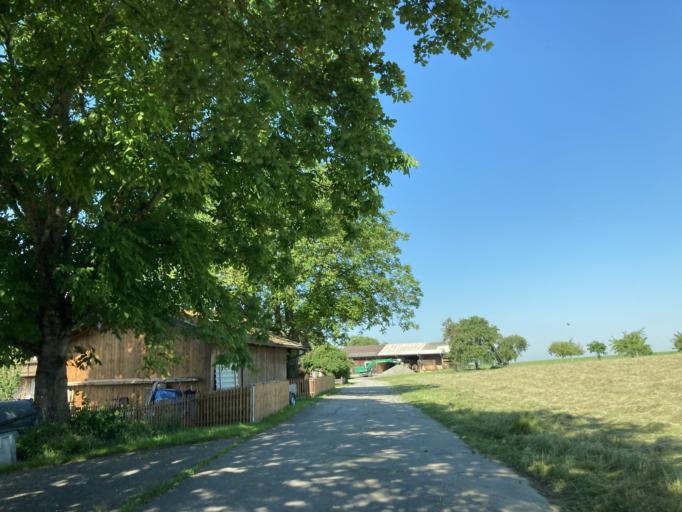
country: DE
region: Bavaria
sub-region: Upper Bavaria
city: Hoslwang
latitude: 47.9659
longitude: 12.3251
